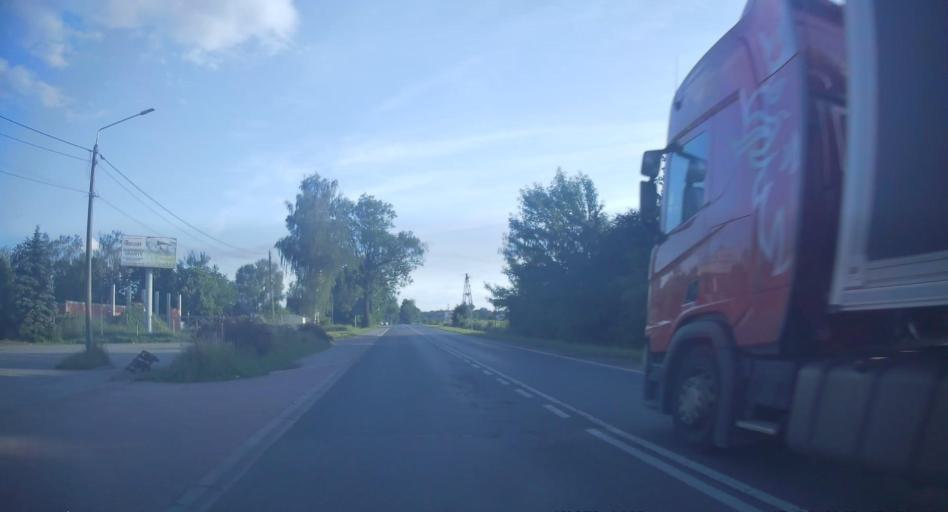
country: PL
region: Silesian Voivodeship
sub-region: Powiat bierunsko-ledzinski
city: Chelm Slaski
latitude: 50.0878
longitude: 19.2015
